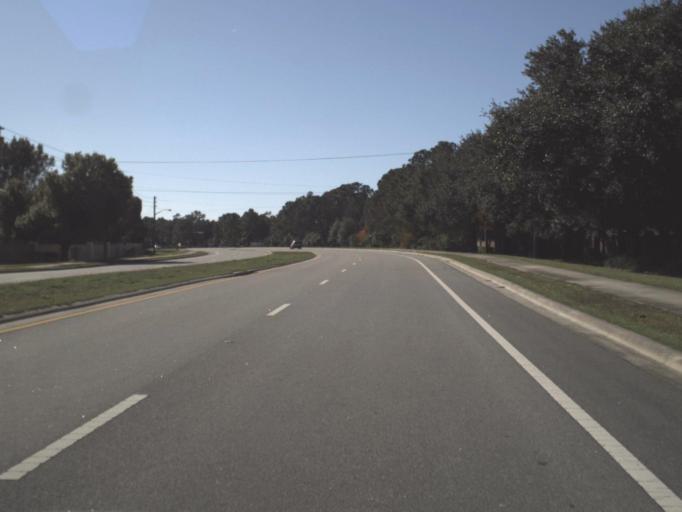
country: US
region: Florida
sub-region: Volusia County
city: Ormond Beach
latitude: 29.2652
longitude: -81.0942
